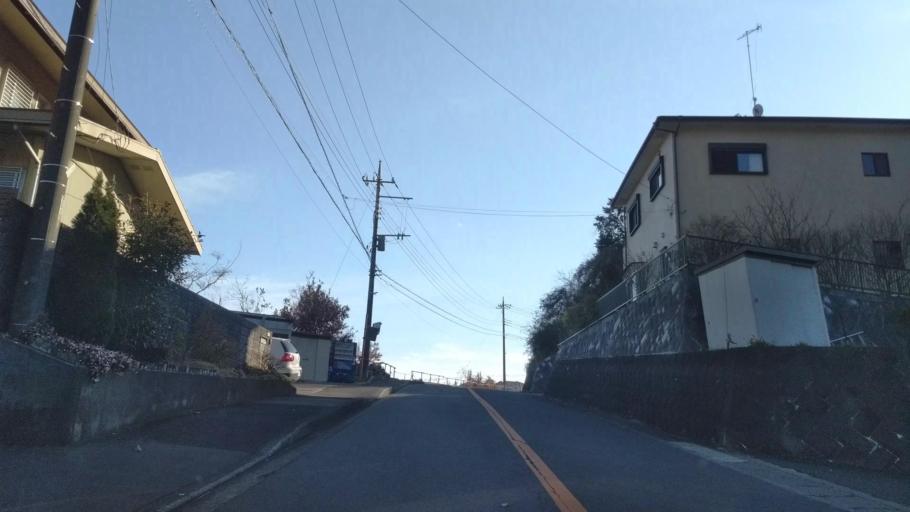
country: JP
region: Kanagawa
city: Hadano
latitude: 35.3685
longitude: 139.2520
